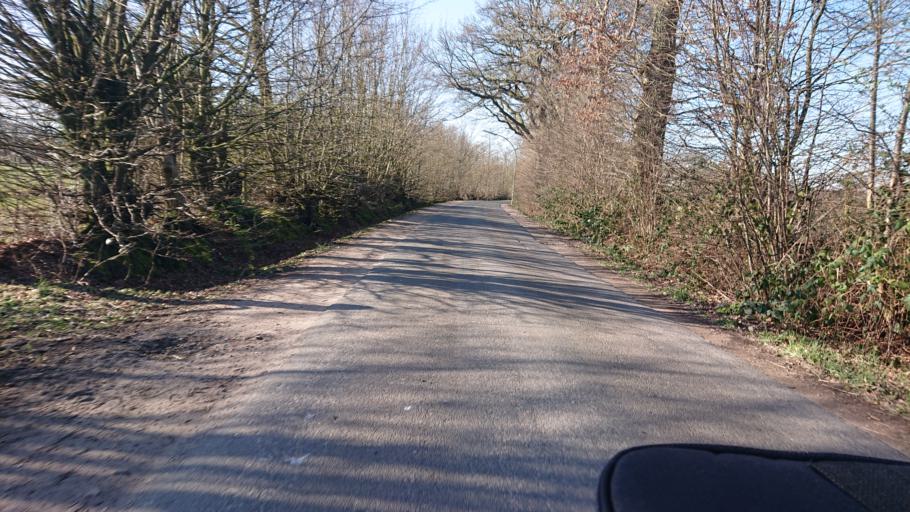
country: DE
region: Schleswig-Holstein
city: Hasloh
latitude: 53.6594
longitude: 9.8915
